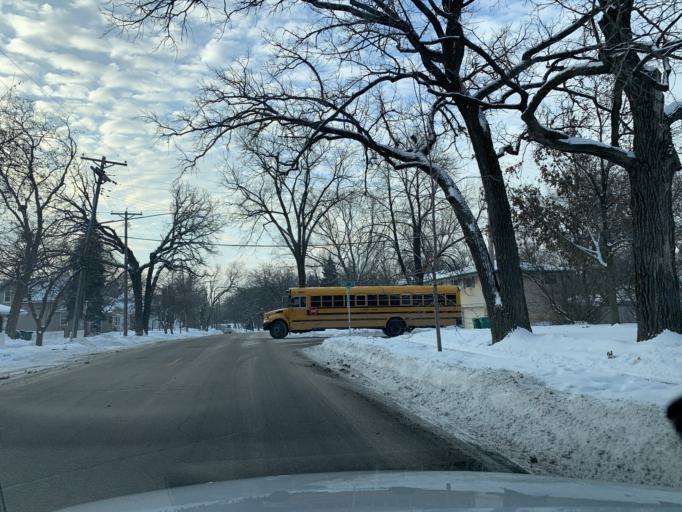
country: US
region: Minnesota
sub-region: Hennepin County
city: Saint Louis Park
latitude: 44.9264
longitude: -93.3558
